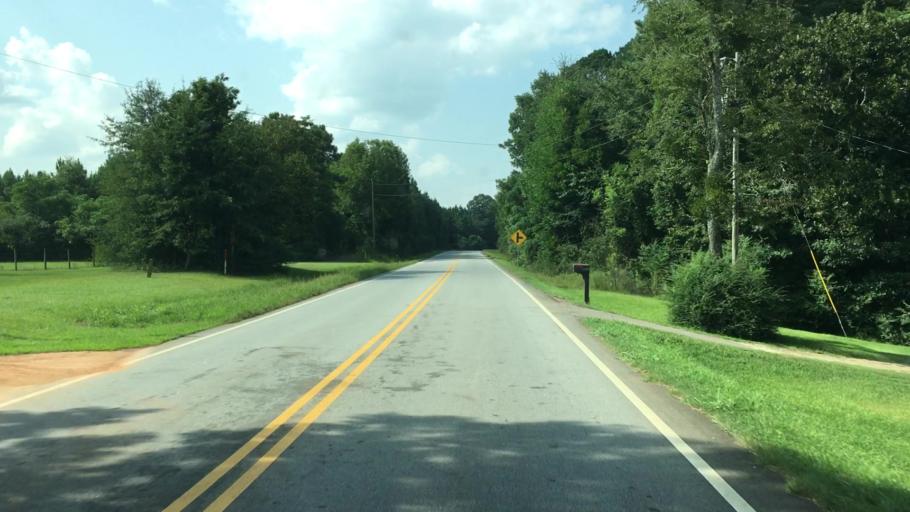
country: US
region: Georgia
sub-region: Jasper County
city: Monticello
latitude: 33.3611
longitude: -83.7513
